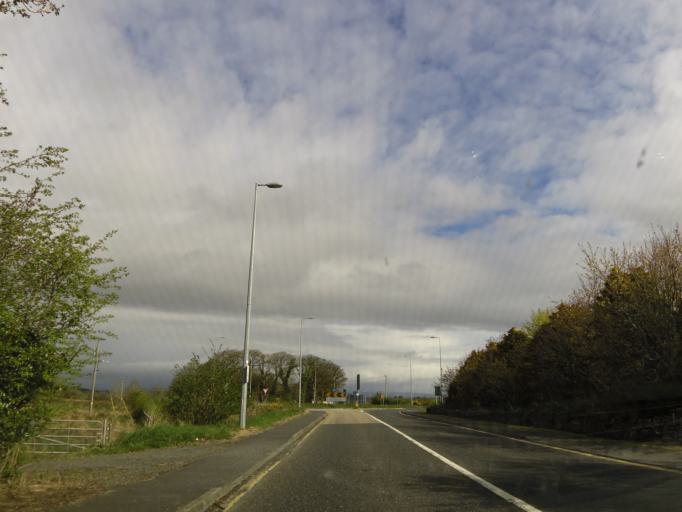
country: IE
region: Connaught
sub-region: Sligo
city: Tobercurry
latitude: 53.9545
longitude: -8.7933
